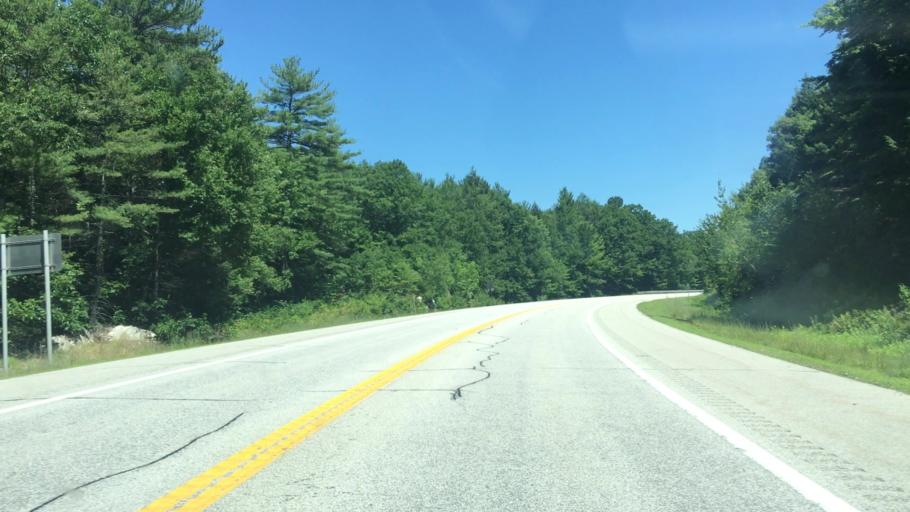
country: US
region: New Hampshire
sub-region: Merrimack County
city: Contoocook
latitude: 43.1807
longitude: -71.7370
